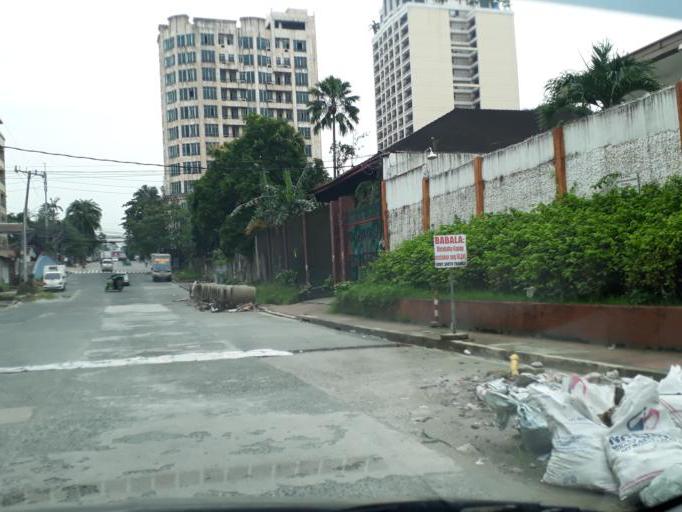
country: PH
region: Metro Manila
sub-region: Quezon City
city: Quezon City
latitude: 14.6413
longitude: 121.0353
